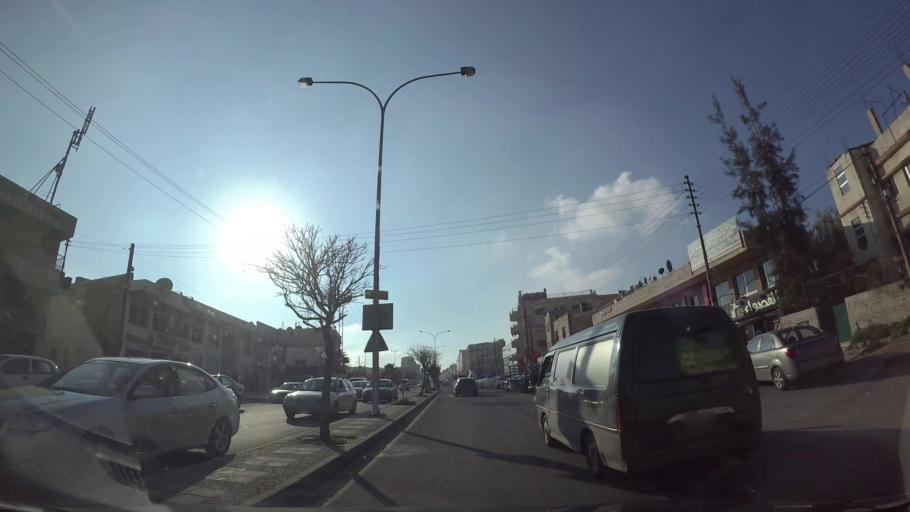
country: JO
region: Amman
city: Amman
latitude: 31.9755
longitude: 35.9591
